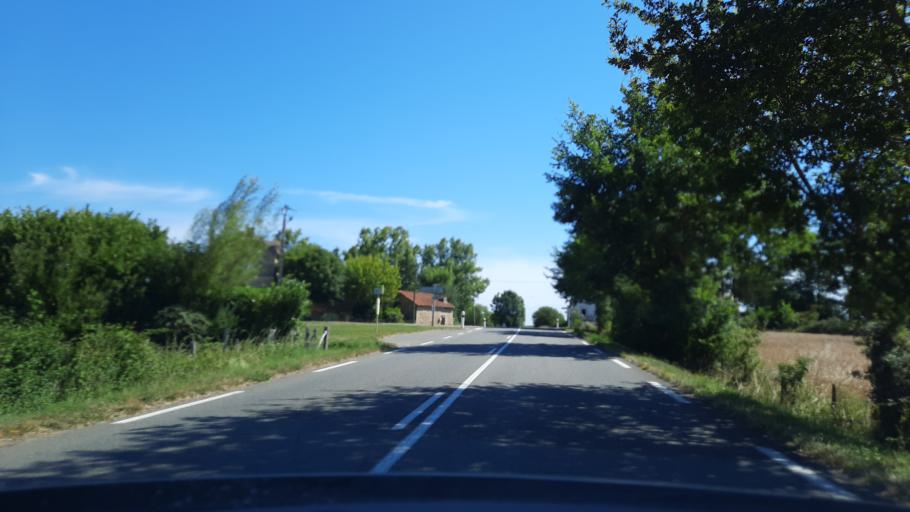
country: FR
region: Midi-Pyrenees
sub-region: Departement de l'Aveyron
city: Montbazens
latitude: 44.4511
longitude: 2.2141
